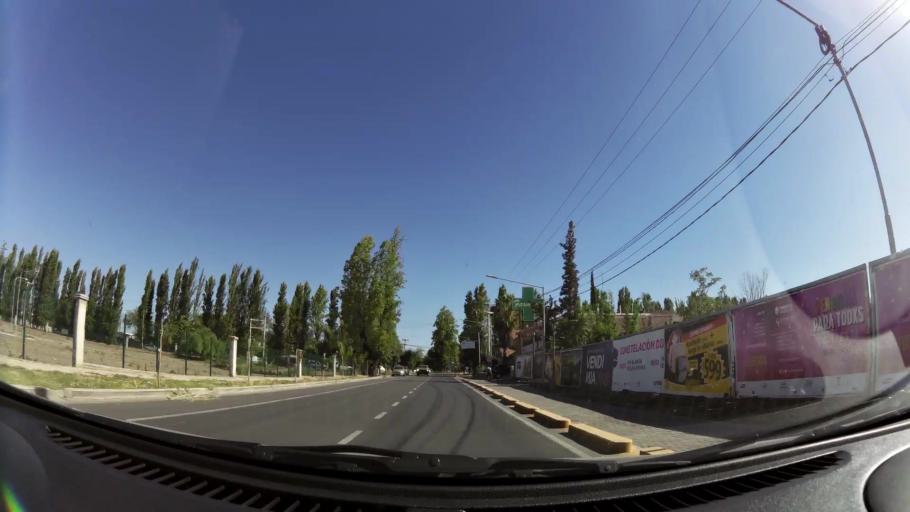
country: AR
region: Mendoza
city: Villa Nueva
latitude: -32.9200
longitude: -68.8006
